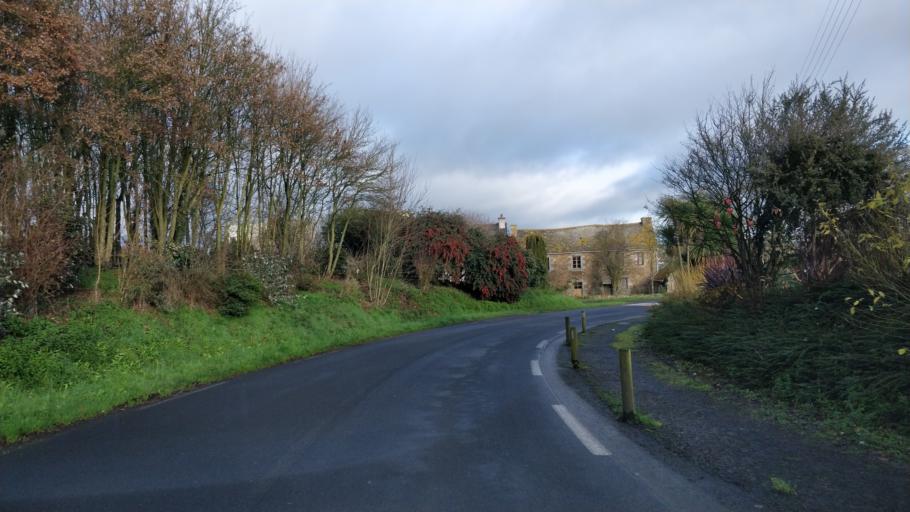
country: FR
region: Brittany
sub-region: Departement des Cotes-d'Armor
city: Lamballe
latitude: 48.4622
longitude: -2.5319
